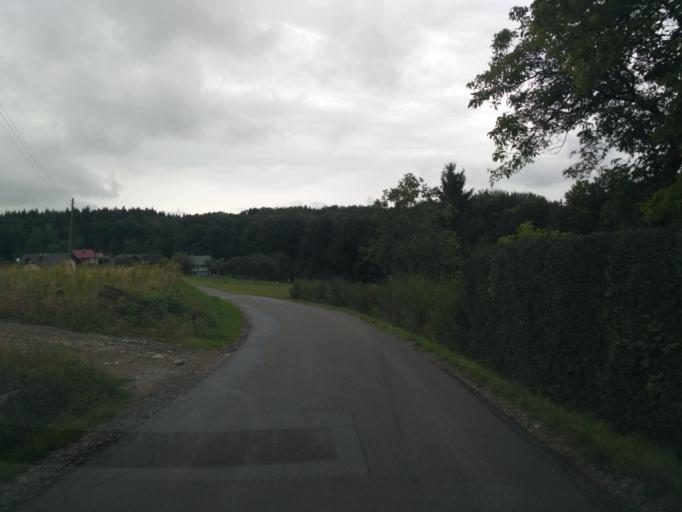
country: PL
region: Subcarpathian Voivodeship
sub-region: Powiat strzyzowski
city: Strzyzow
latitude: 49.8897
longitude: 21.7895
